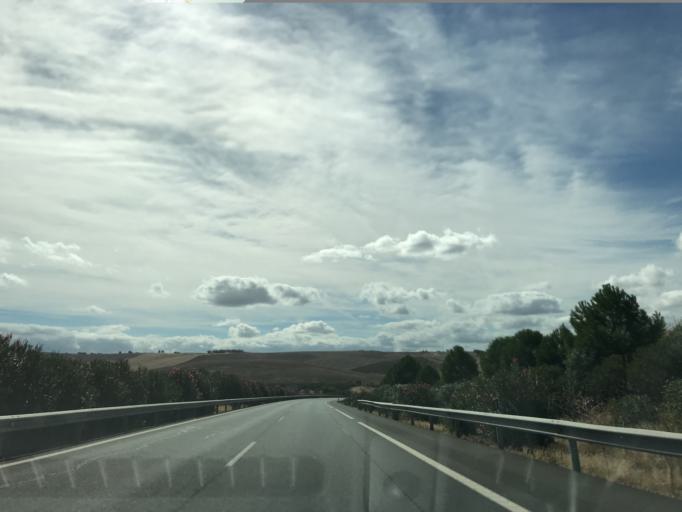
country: ES
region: Andalusia
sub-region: Province of Cordoba
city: La Victoria
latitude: 37.7398
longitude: -4.8500
